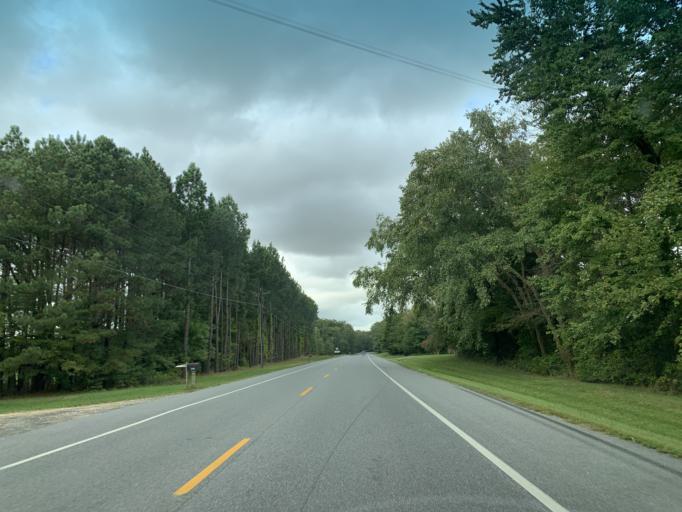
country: US
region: Maryland
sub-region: Caroline County
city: Ridgely
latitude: 39.0201
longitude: -75.8751
